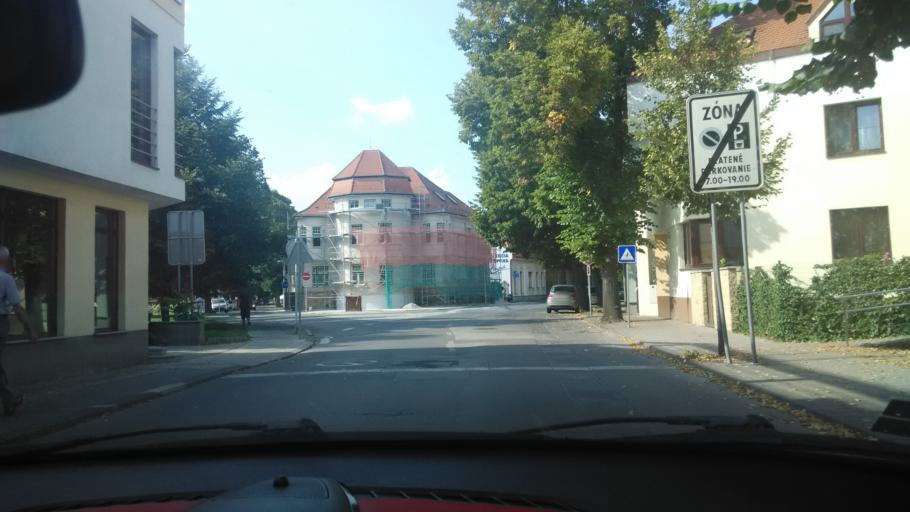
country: SK
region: Trnavsky
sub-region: Okres Trnava
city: Piestany
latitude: 48.5931
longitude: 17.8341
